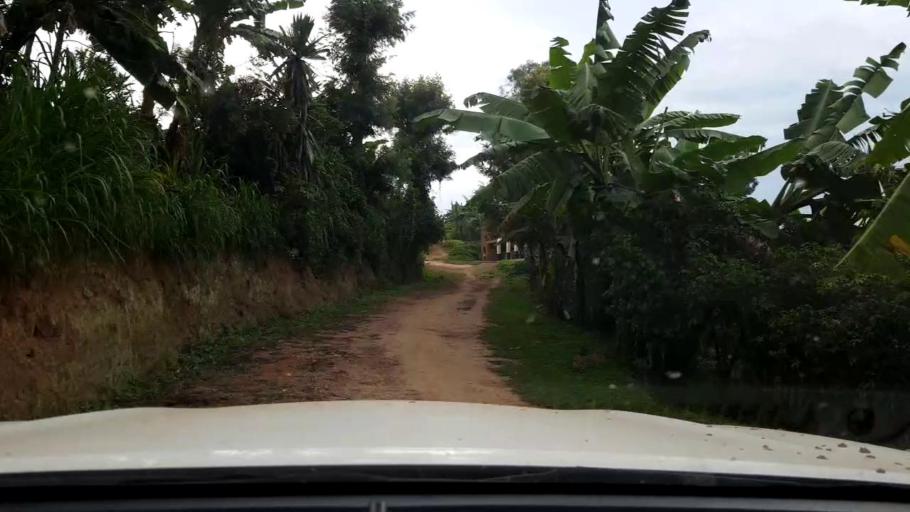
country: RW
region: Western Province
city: Kibuye
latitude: -2.0015
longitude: 29.3704
